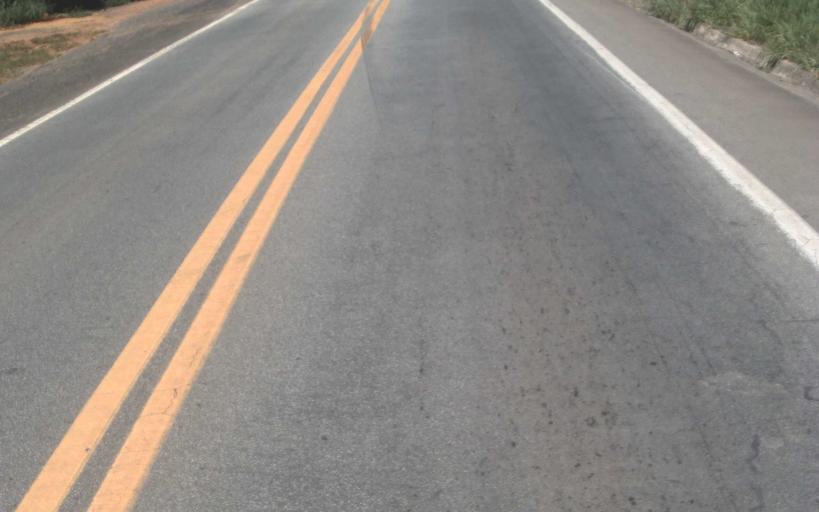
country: BR
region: Minas Gerais
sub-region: Ipaba
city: Ipaba
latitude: -19.3599
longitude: -42.4417
